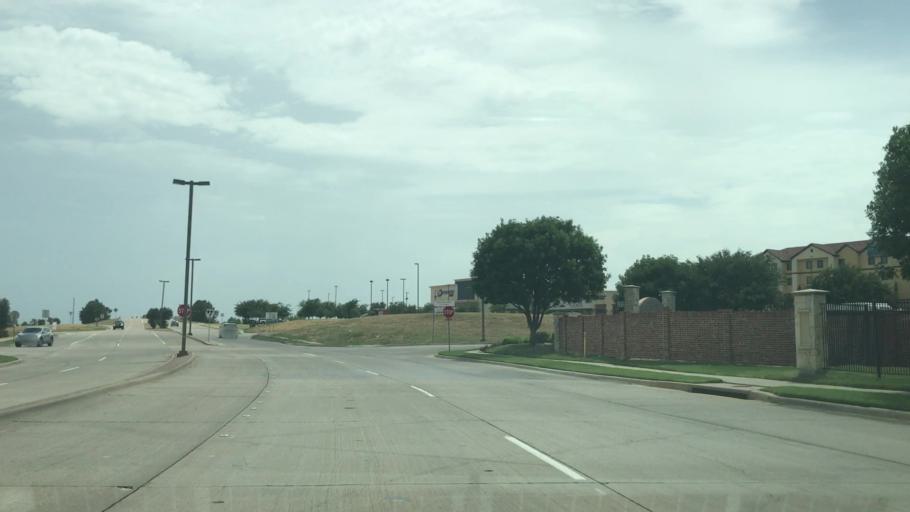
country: US
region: Texas
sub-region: Dallas County
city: Coppell
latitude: 32.9231
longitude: -96.9738
